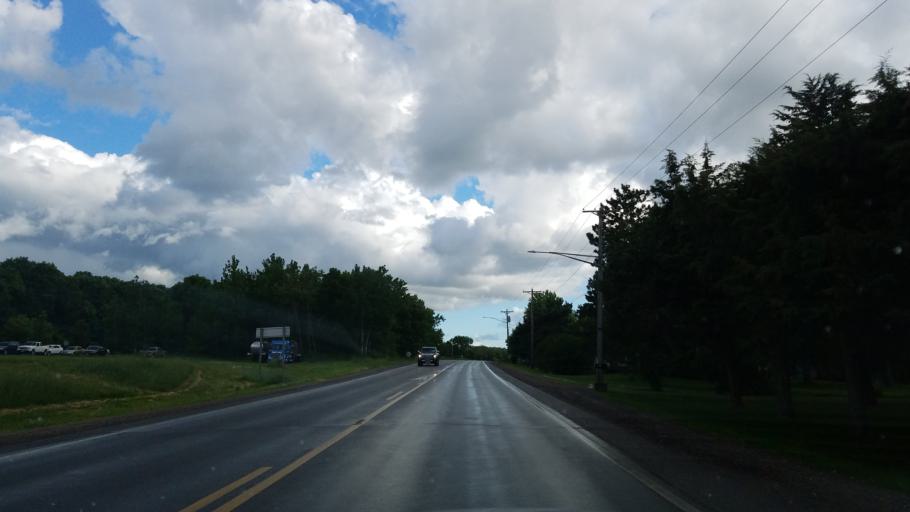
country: US
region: Wisconsin
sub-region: Polk County
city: Saint Croix Falls
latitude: 45.3527
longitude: -92.6377
